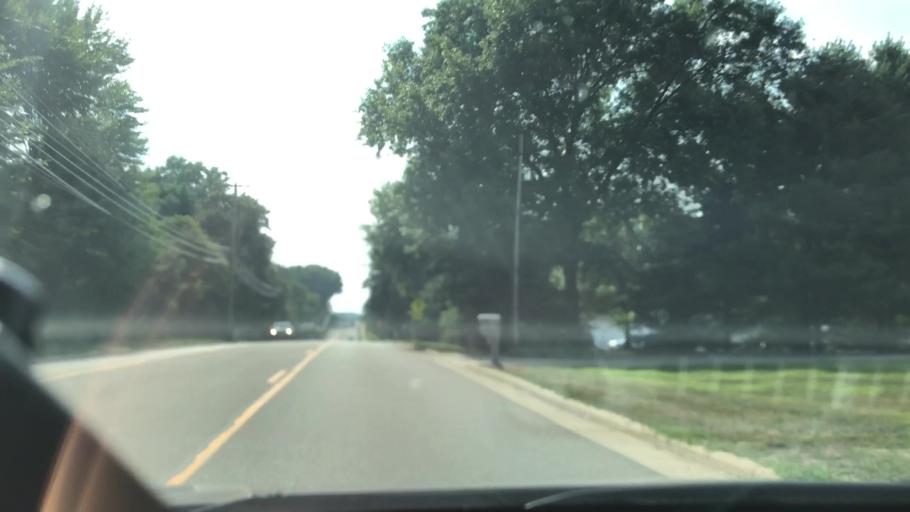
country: US
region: Ohio
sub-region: Summit County
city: Green
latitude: 40.9596
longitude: -81.4784
